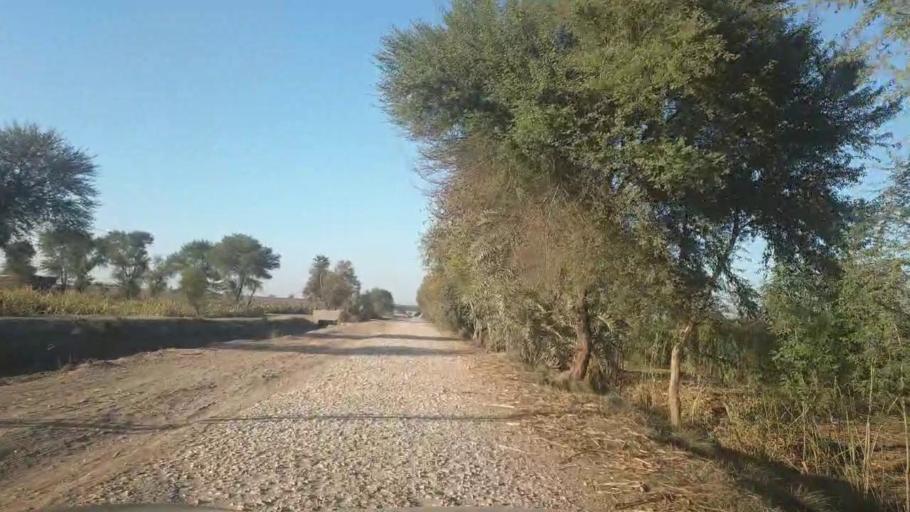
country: PK
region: Sindh
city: Ghotki
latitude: 28.0040
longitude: 69.2701
